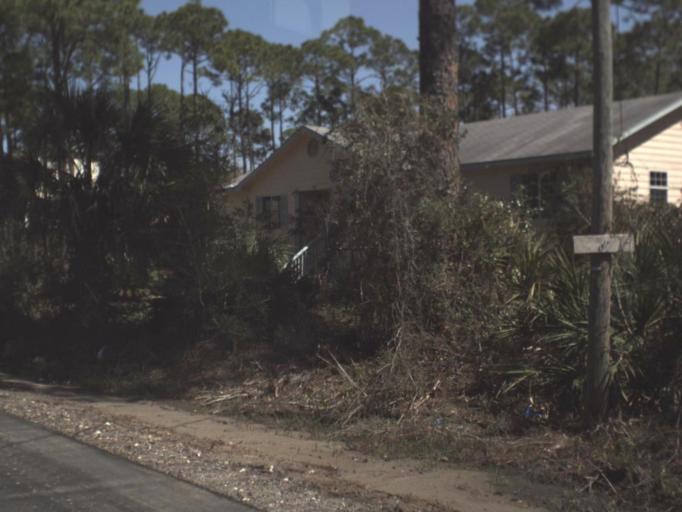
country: US
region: Florida
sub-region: Gulf County
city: Port Saint Joe
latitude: 29.7008
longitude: -85.3060
